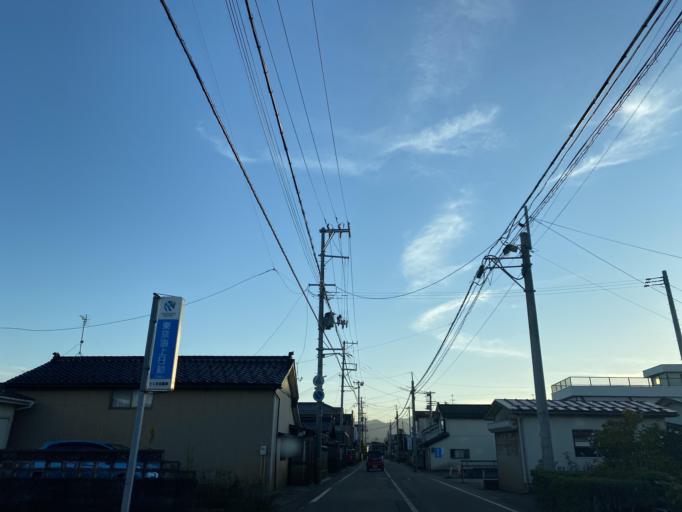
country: JP
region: Niigata
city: Kashiwazaki
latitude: 37.3781
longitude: 138.5659
